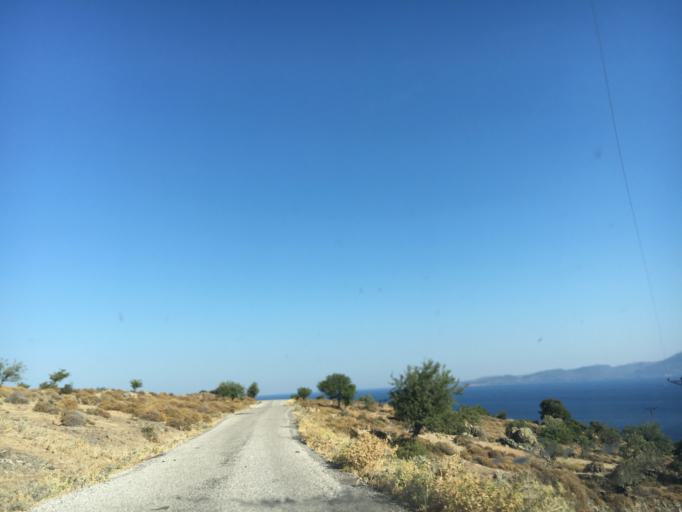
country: TR
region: Canakkale
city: Behram
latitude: 39.4897
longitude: 26.2598
